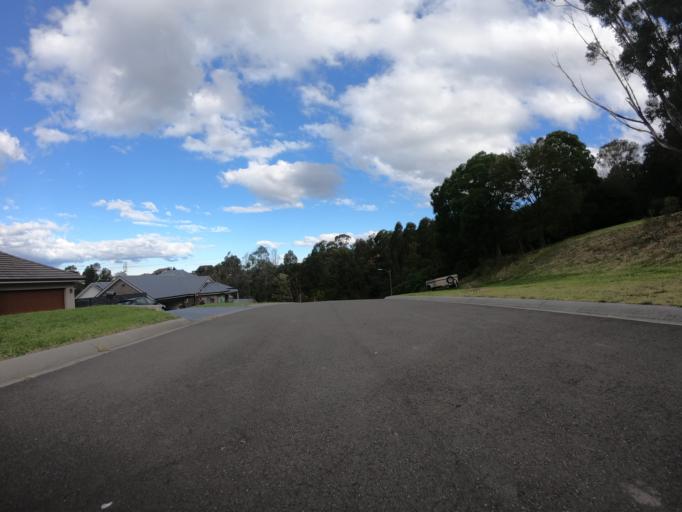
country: AU
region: New South Wales
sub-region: Wollongong
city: Mount Keira
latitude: -34.4198
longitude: 150.8512
